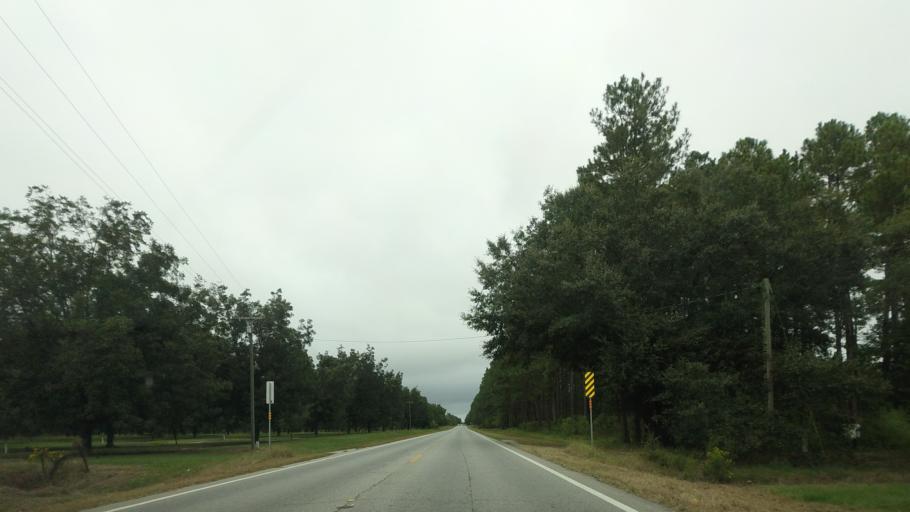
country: US
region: Georgia
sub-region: Berrien County
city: Ray City
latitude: 31.0988
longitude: -83.2075
